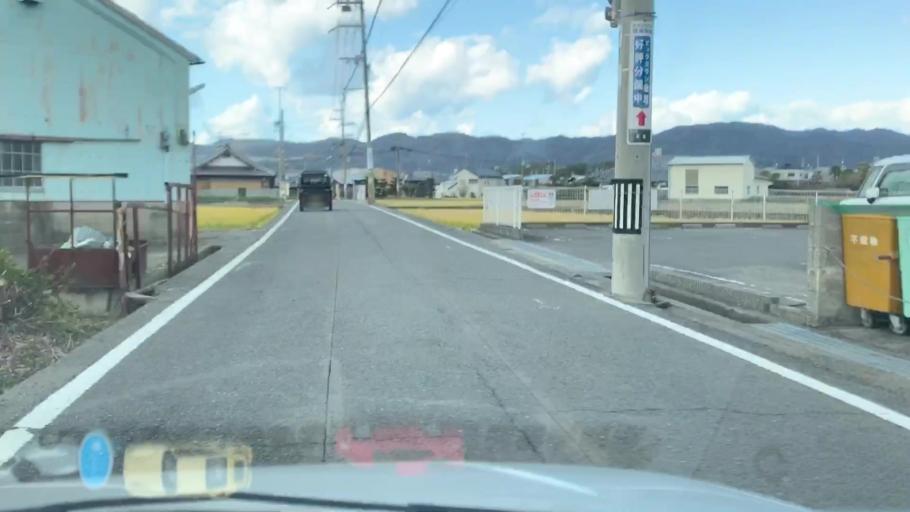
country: JP
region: Wakayama
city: Iwade
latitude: 34.2636
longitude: 135.2980
